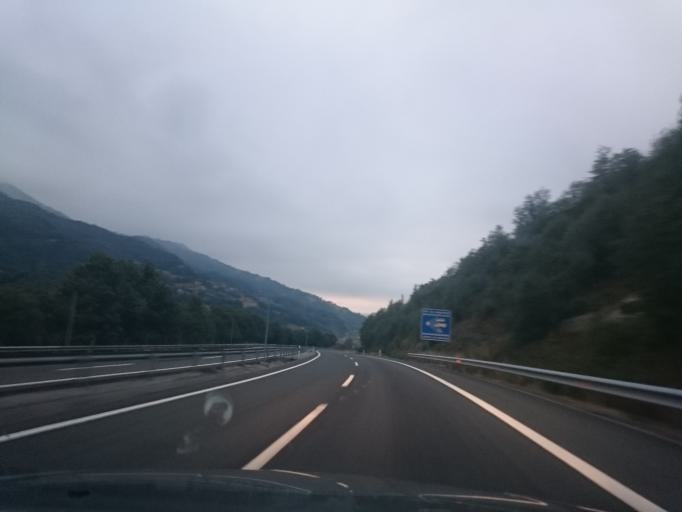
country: ES
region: Asturias
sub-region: Province of Asturias
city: Pola de Lena
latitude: 43.0925
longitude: -5.8227
